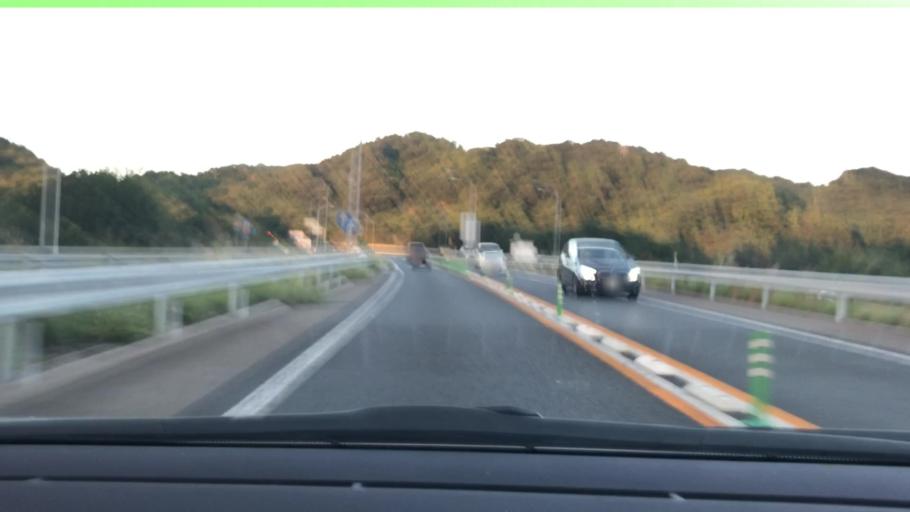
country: JP
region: Hiroshima
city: Innoshima
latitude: 34.3372
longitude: 133.1598
